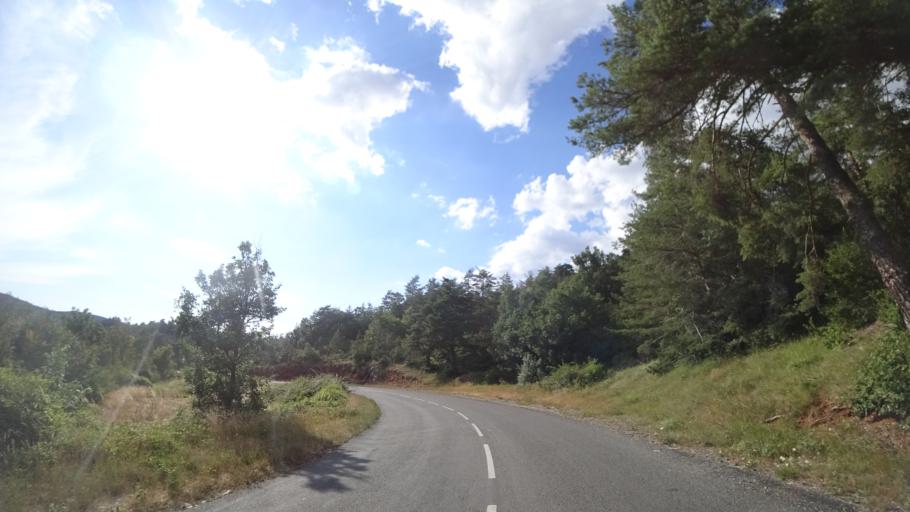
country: FR
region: Languedoc-Roussillon
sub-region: Departement de la Lozere
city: Chanac
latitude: 44.3797
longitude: 3.3224
